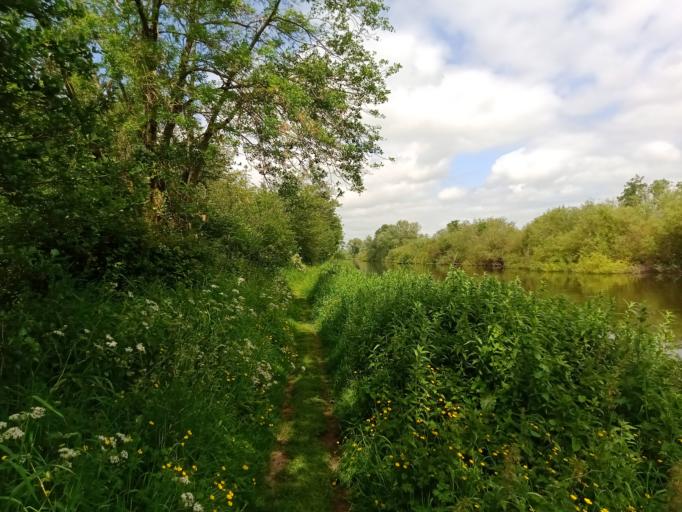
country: IE
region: Leinster
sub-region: County Carlow
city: Carlow
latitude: 52.7951
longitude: -6.9610
